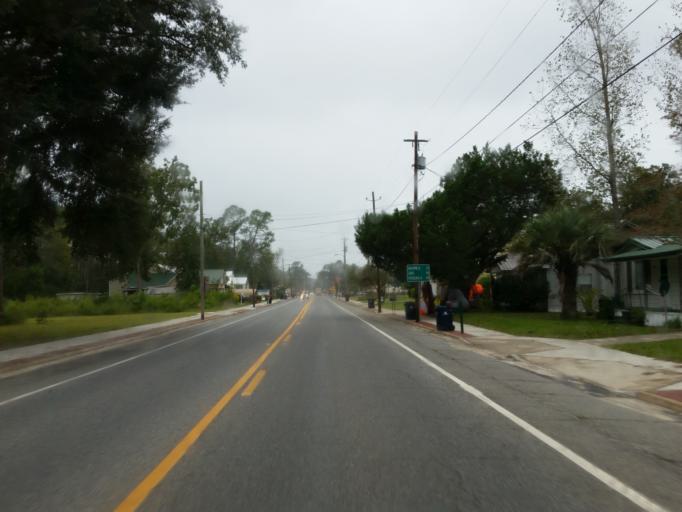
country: US
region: Georgia
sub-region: Berrien County
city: Ray City
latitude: 31.0756
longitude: -83.1940
